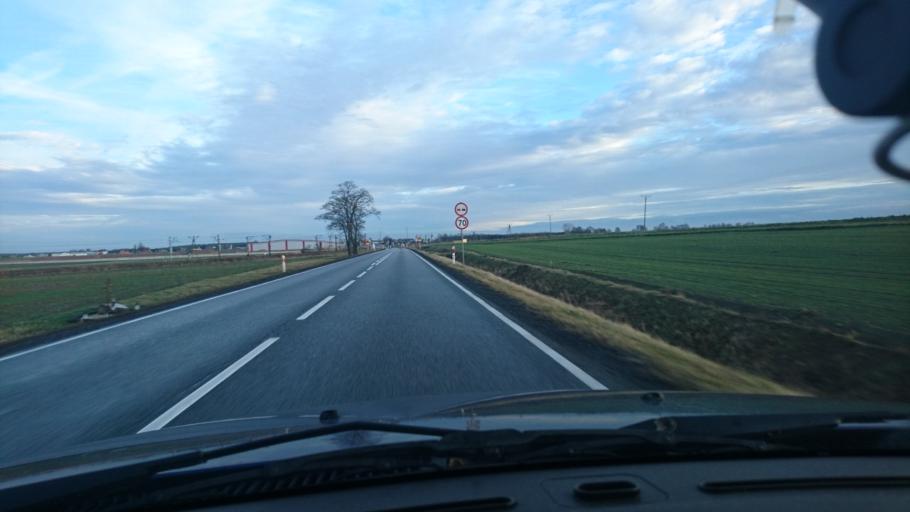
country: PL
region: Greater Poland Voivodeship
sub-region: Powiat kepinski
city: Slupia pod Kepnem
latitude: 51.2337
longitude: 18.0608
